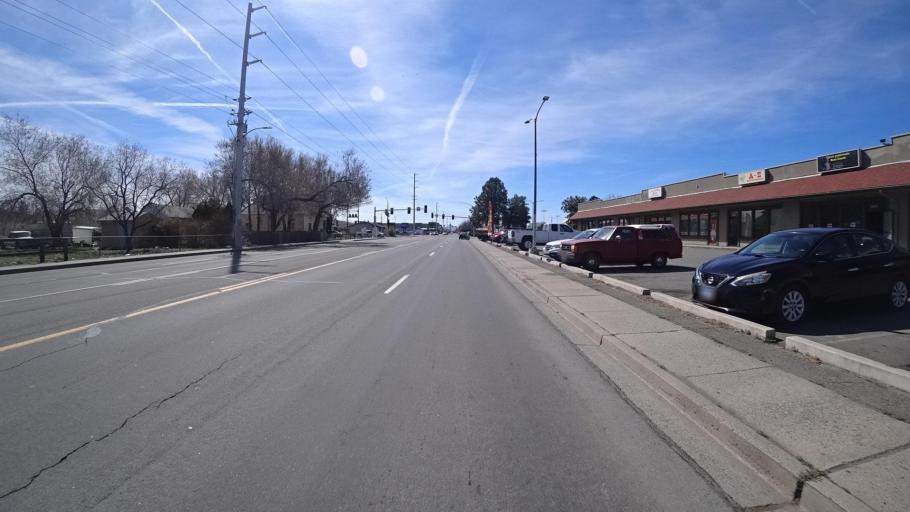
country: US
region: Nevada
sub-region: Washoe County
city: Sparks
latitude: 39.5480
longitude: -119.7714
